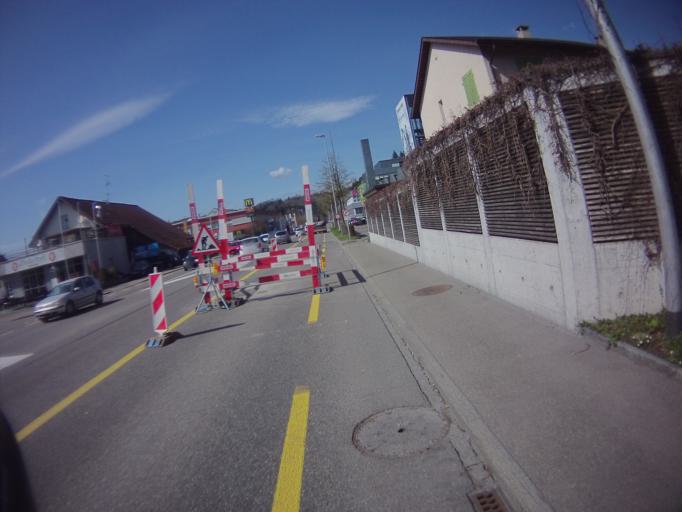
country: CH
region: Aargau
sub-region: Bezirk Baden
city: Baden
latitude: 47.4504
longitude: 8.2912
